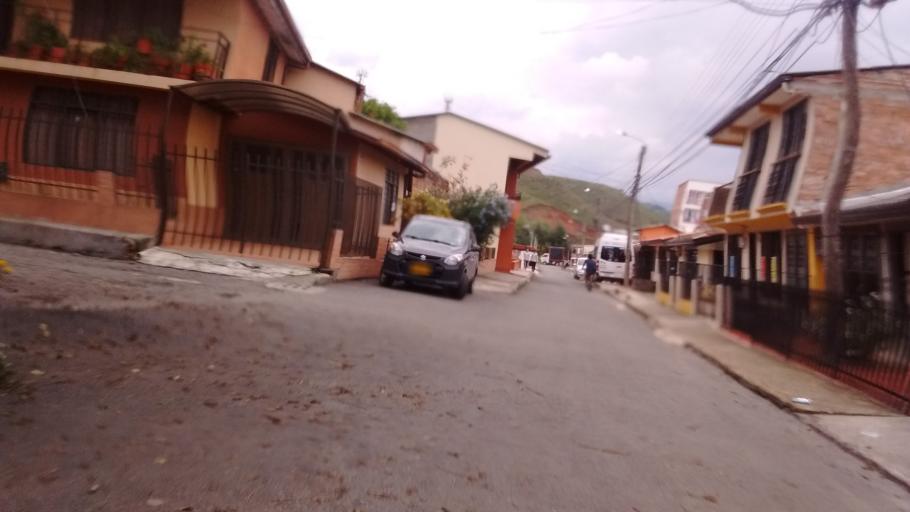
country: CO
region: Cauca
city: Popayan
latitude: 2.4555
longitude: -76.5904
